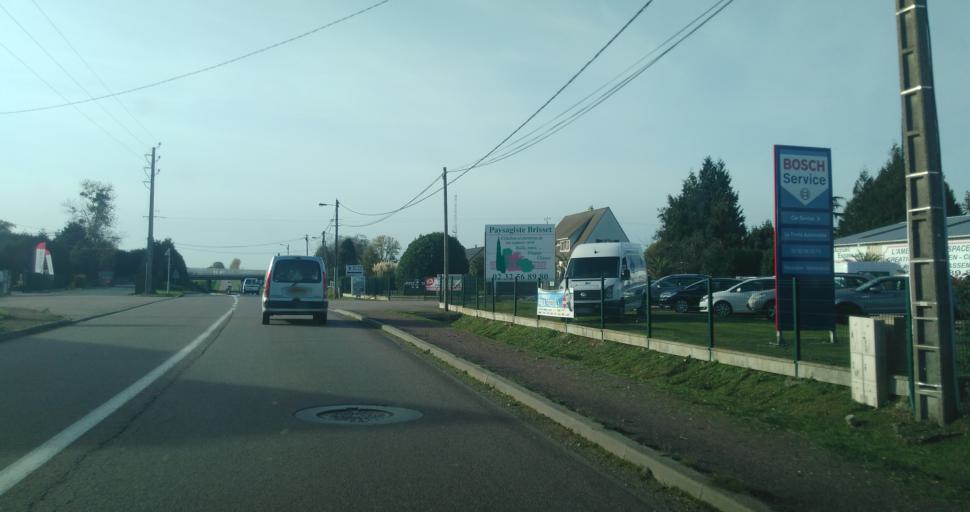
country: FR
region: Haute-Normandie
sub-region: Departement de l'Eure
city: Saint-Ouen-de-Thouberville
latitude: 49.3585
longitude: 0.8770
